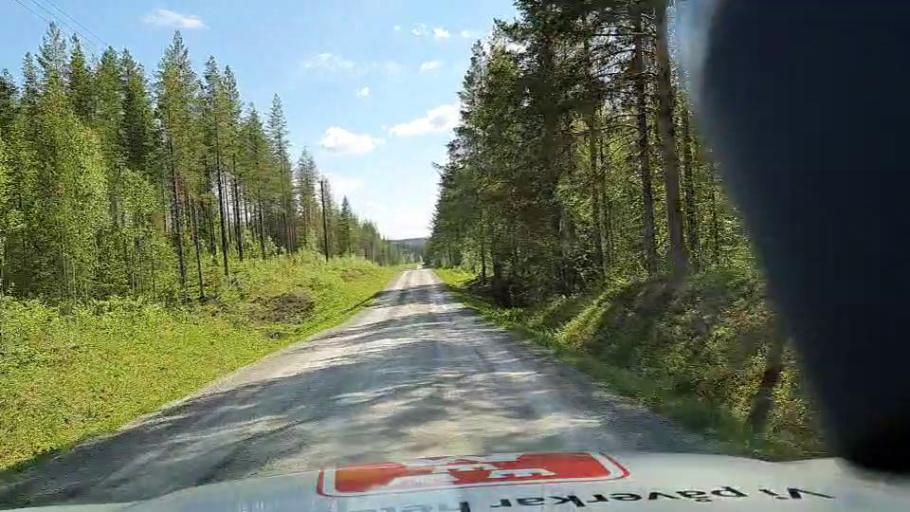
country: SE
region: Jaemtland
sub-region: Stroemsunds Kommun
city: Stroemsund
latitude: 64.4742
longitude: 15.5936
